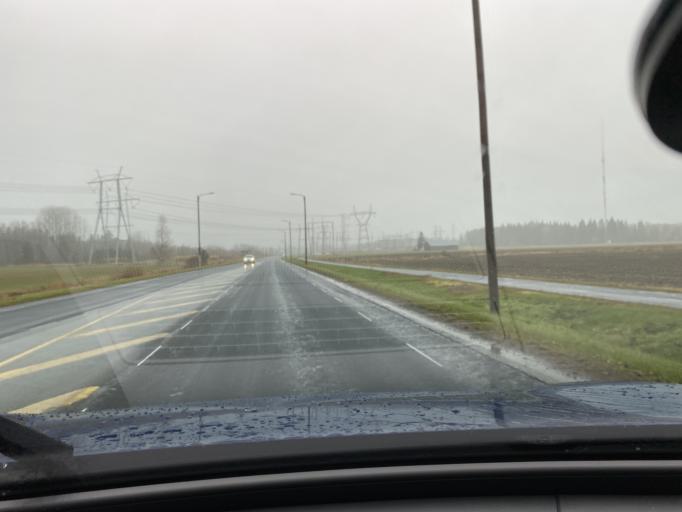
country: FI
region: Haeme
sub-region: Forssa
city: Forssa
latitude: 60.8009
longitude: 23.5876
